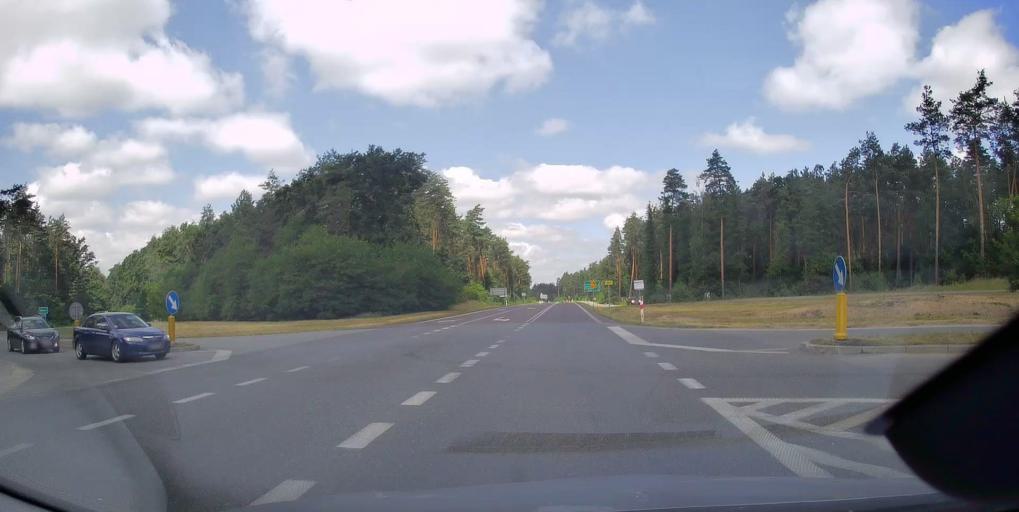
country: PL
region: Subcarpathian Voivodeship
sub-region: Powiat mielecki
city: Mielec
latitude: 50.3157
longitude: 21.5022
